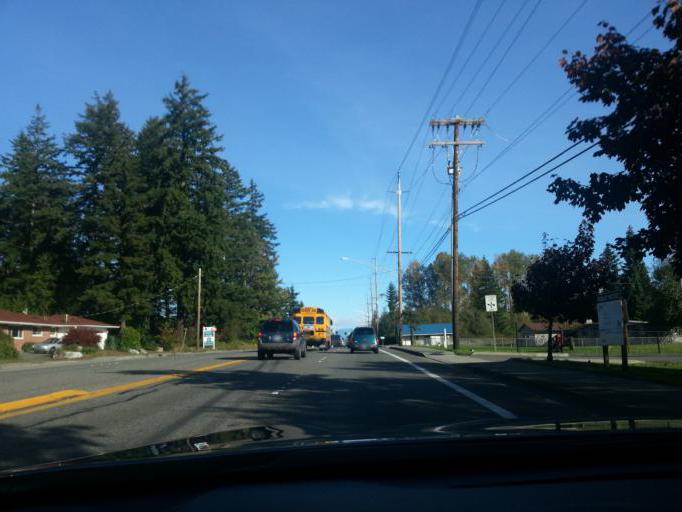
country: US
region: Washington
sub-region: Snohomish County
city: Mill Creek
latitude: 47.8780
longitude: -122.2024
